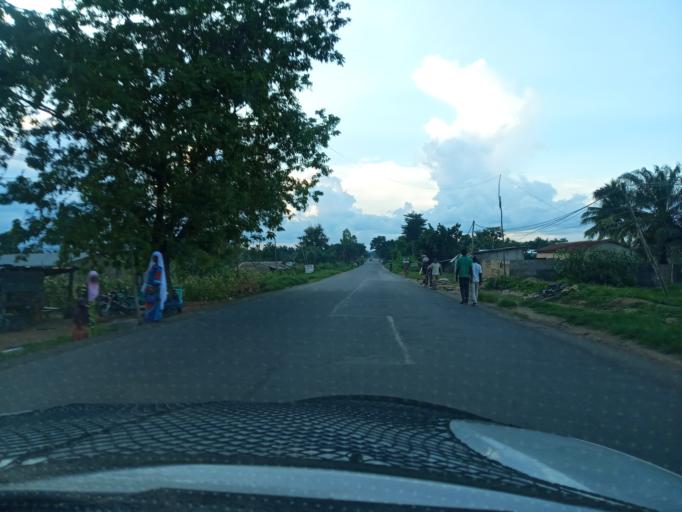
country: TG
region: Centrale
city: Sokode
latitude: 8.8375
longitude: 1.0771
